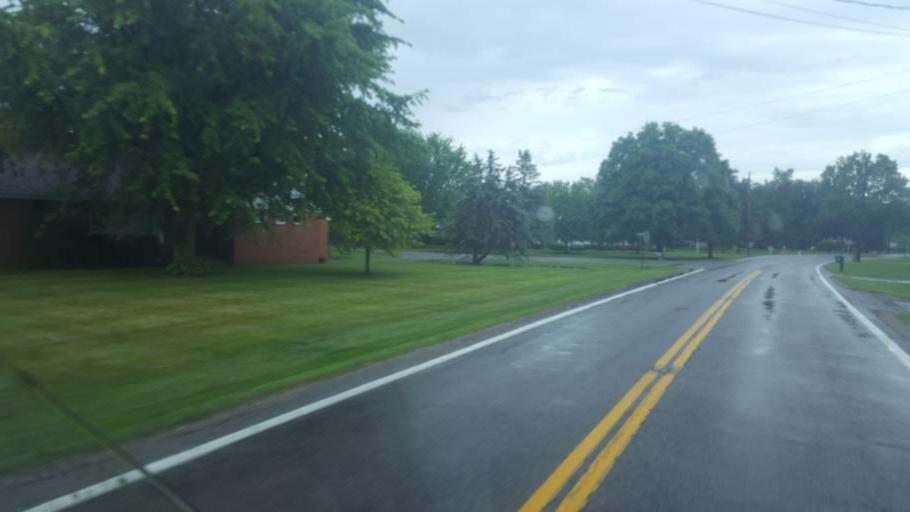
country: US
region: Ohio
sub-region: Marion County
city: Marion
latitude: 40.5667
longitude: -83.0868
